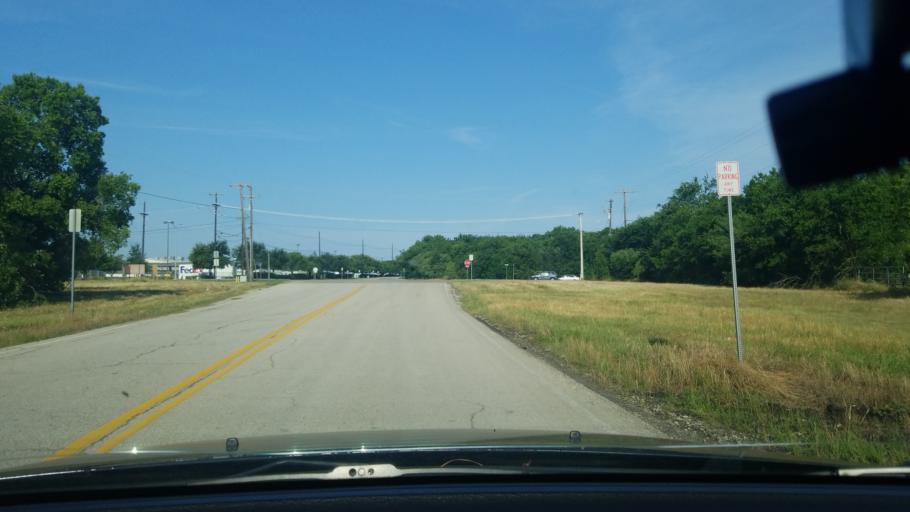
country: US
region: Texas
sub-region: Dallas County
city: Sunnyvale
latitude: 32.7728
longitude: -96.5602
